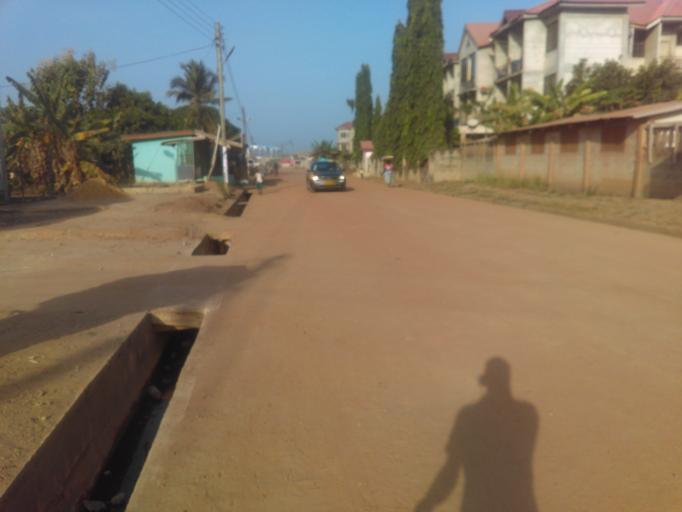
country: GH
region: Central
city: Cape Coast
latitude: 5.1093
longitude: -1.2962
